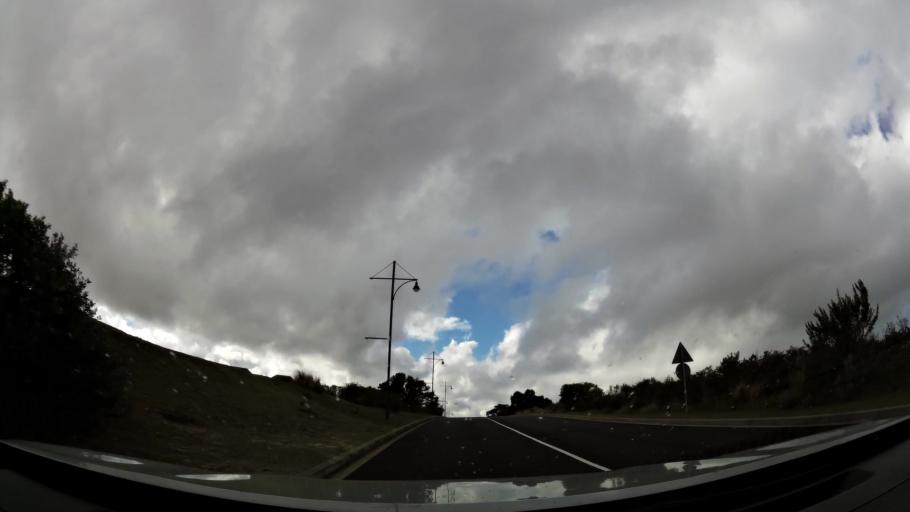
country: ZA
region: Western Cape
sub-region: Eden District Municipality
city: Knysna
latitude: -34.0665
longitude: 23.1000
